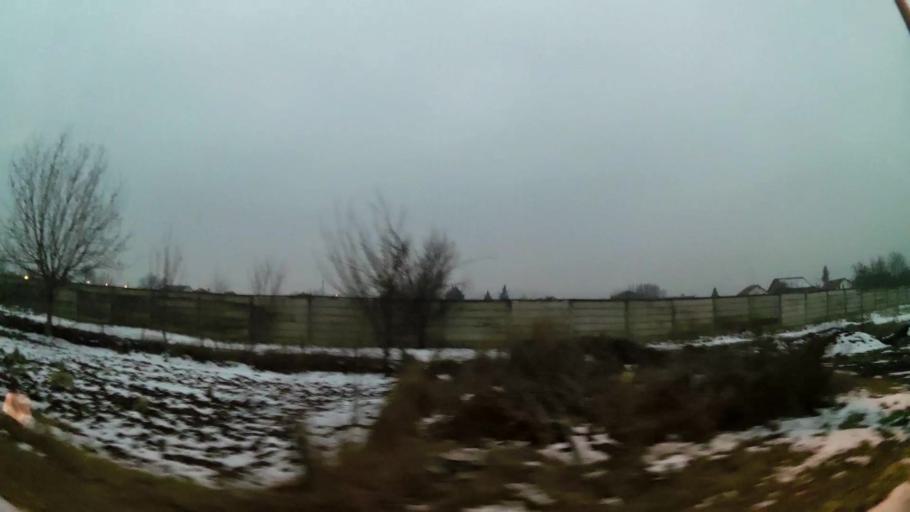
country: MK
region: Kisela Voda
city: Kisela Voda
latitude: 41.9691
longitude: 21.4908
